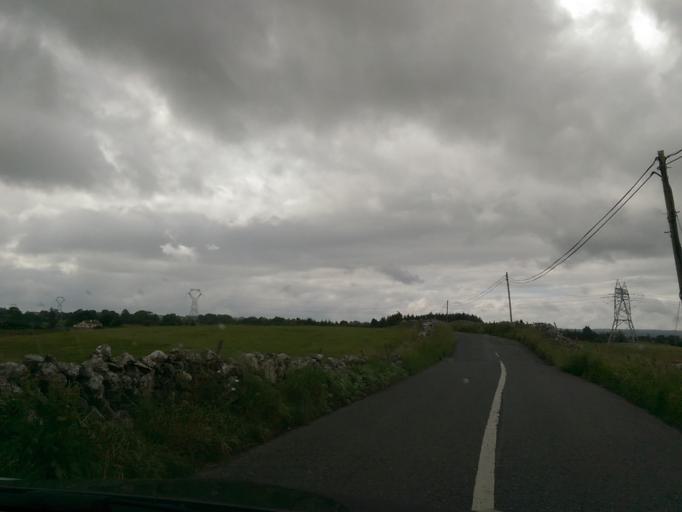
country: IE
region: Connaught
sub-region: County Galway
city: Loughrea
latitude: 53.2264
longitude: -8.5590
